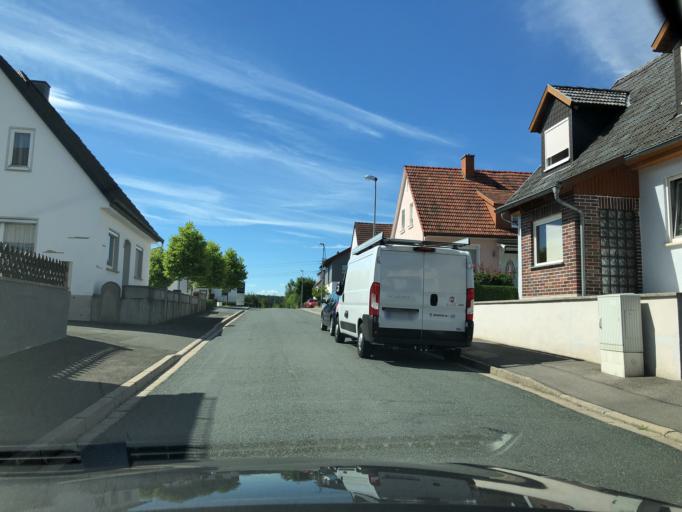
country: DE
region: Bavaria
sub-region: Upper Franconia
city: Sonnefeld
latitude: 50.2151
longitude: 11.0854
